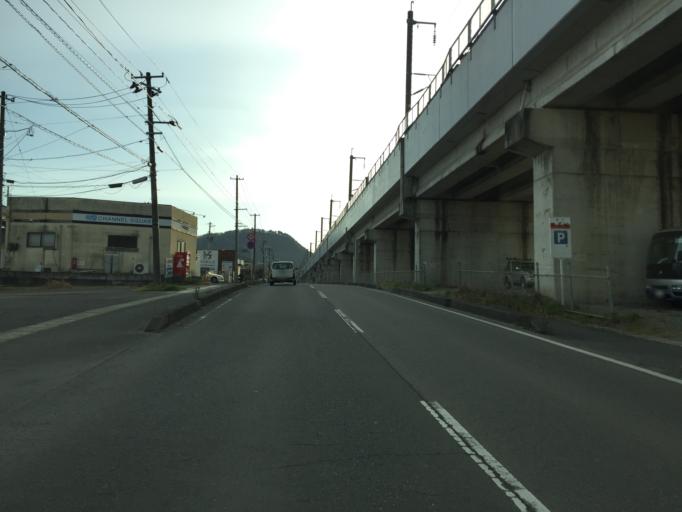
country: JP
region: Fukushima
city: Fukushima-shi
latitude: 37.7877
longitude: 140.4706
